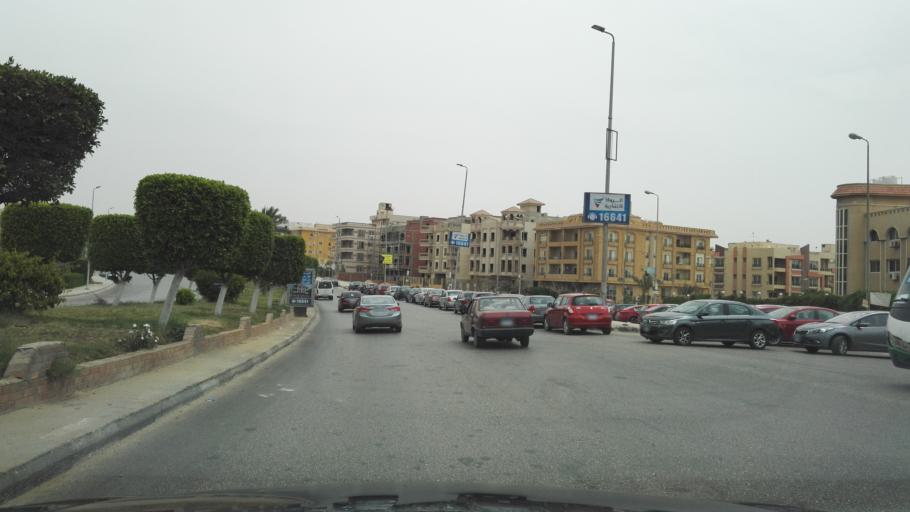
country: EG
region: Muhafazat al Qahirah
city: Cairo
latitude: 29.9912
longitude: 31.4200
